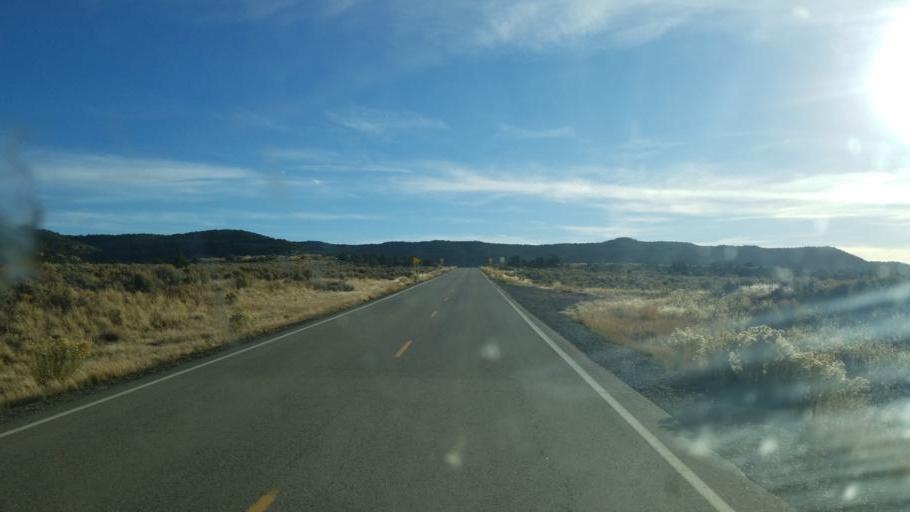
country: US
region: New Mexico
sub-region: San Juan County
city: Bloomfield
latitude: 36.7410
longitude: -107.6214
